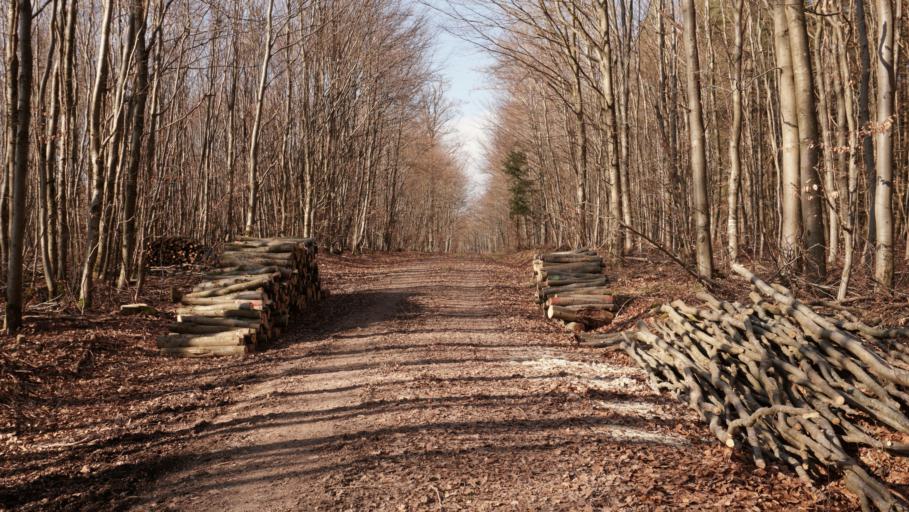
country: DE
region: Baden-Wuerttemberg
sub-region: Karlsruhe Region
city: Fahrenbach
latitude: 49.4517
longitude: 9.1343
